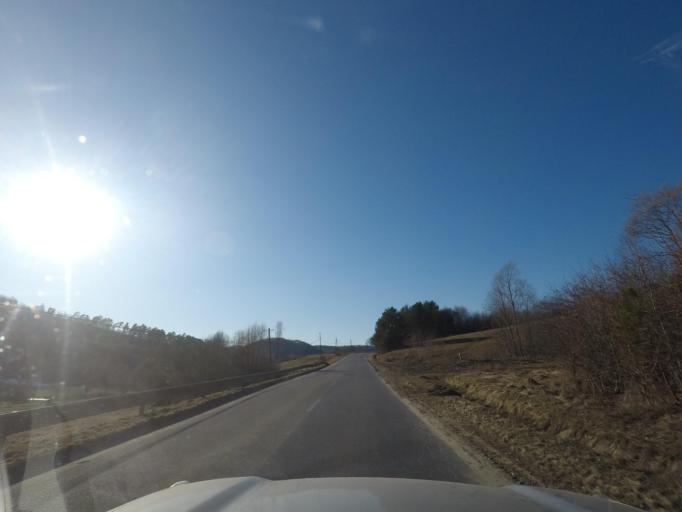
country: SK
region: Presovsky
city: Medzilaborce
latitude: 49.2498
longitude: 21.9249
